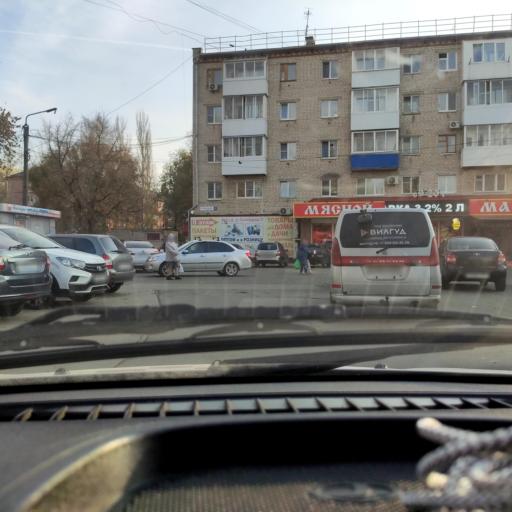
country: RU
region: Samara
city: Tol'yatti
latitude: 53.5055
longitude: 49.4173
